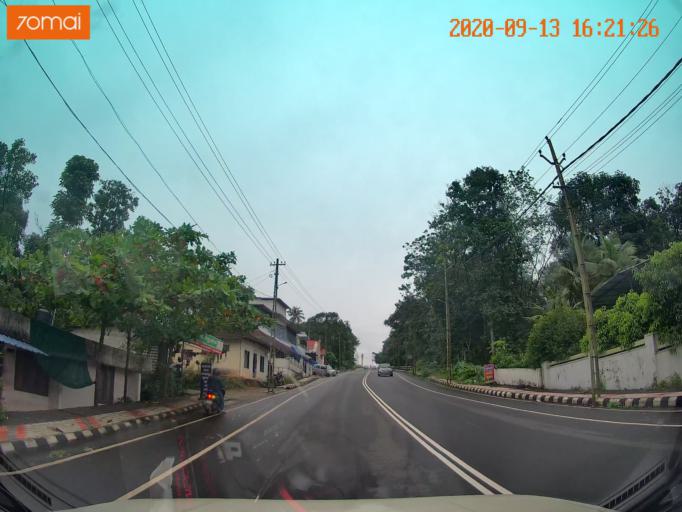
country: IN
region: Kerala
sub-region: Kottayam
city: Lalam
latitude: 9.7086
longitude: 76.6663
